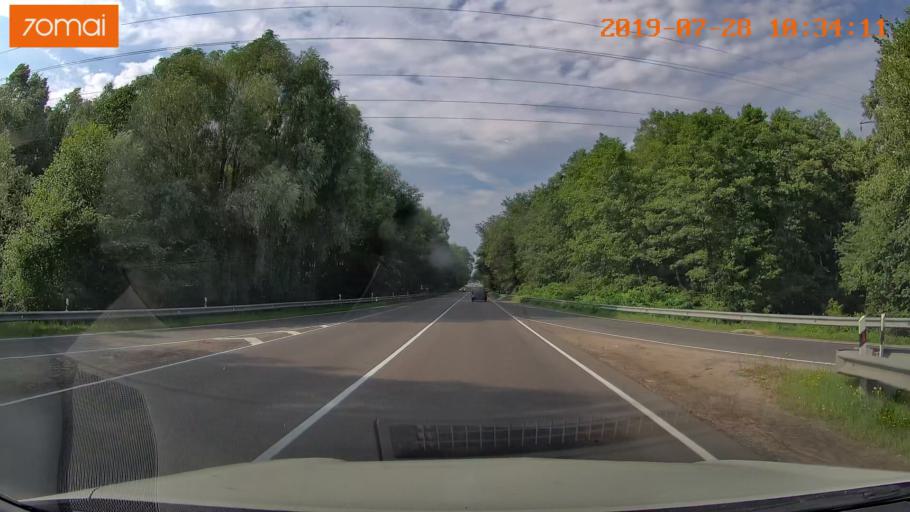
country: RU
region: Kaliningrad
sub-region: Gorod Kaliningrad
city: Kaliningrad
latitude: 54.7558
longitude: 20.4419
